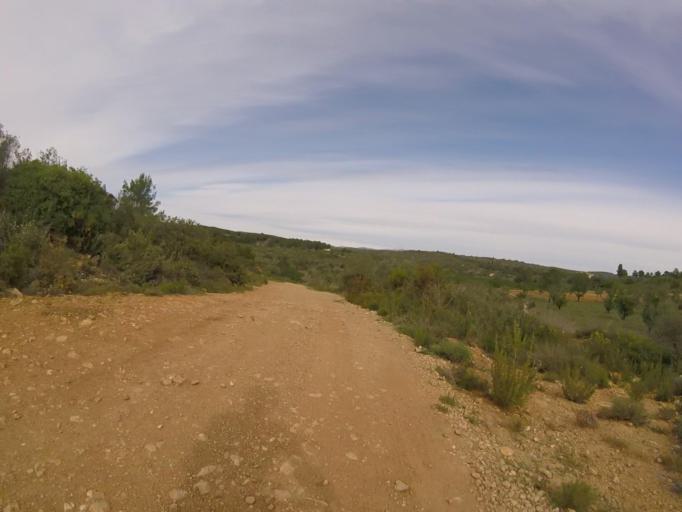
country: ES
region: Valencia
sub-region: Provincia de Castello
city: Torreblanca
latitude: 40.1964
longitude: 0.1305
